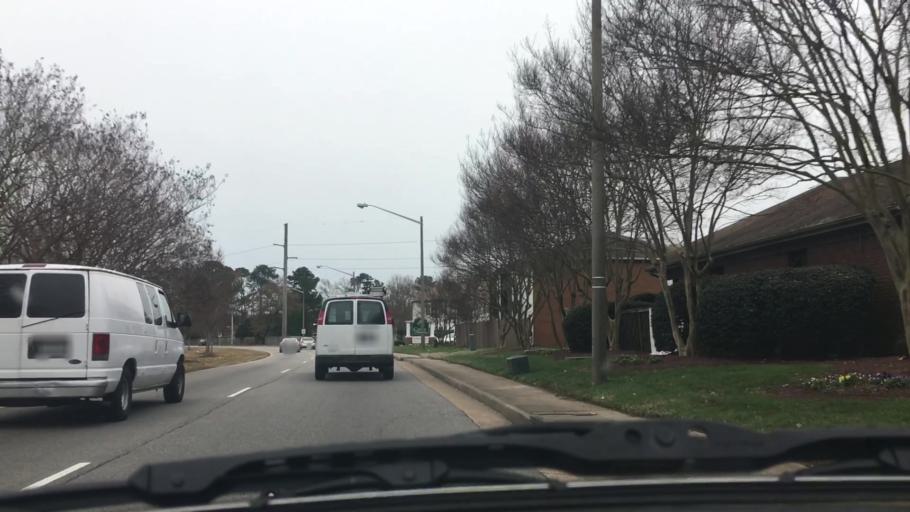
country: US
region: Virginia
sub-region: City of Chesapeake
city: Chesapeake
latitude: 36.8166
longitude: -76.1271
